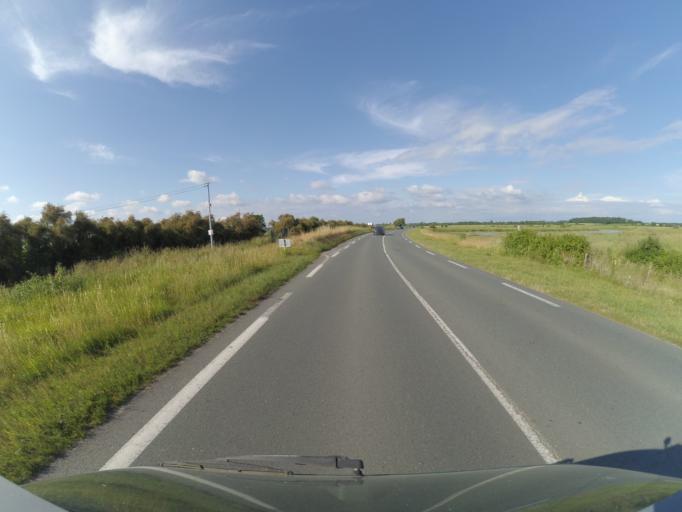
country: FR
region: Poitou-Charentes
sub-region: Departement de la Charente-Maritime
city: Le Gua
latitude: 45.7148
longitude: -0.9724
